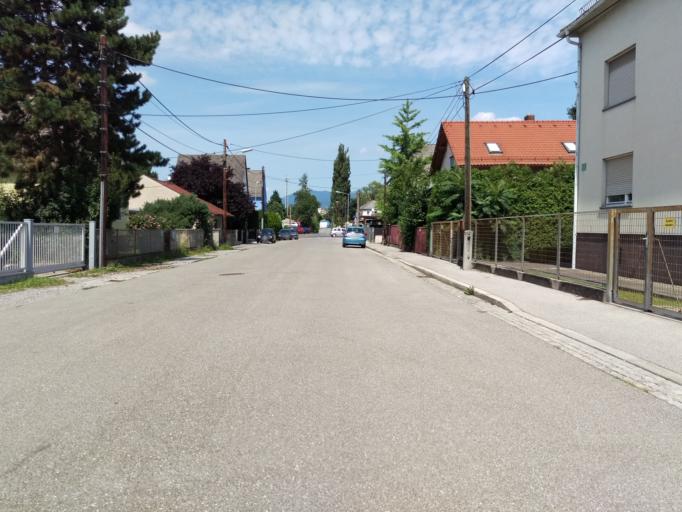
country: AT
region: Styria
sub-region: Graz Stadt
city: Wetzelsdorf
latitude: 47.0582
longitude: 15.4173
